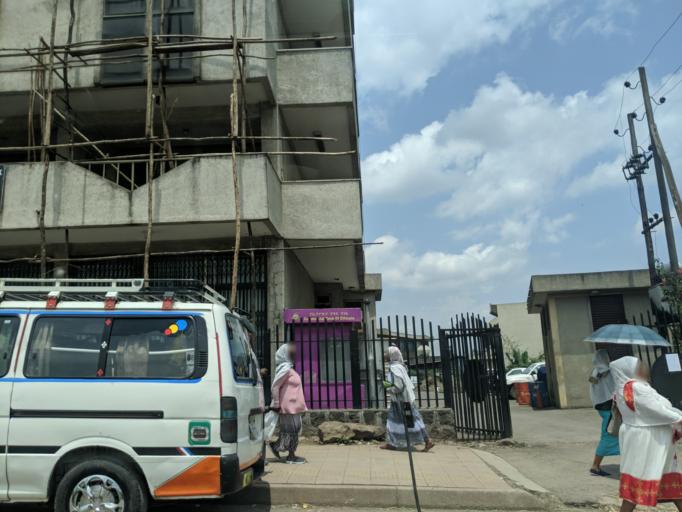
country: ET
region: Adis Abeba
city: Addis Ababa
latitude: 8.9530
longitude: 38.7629
